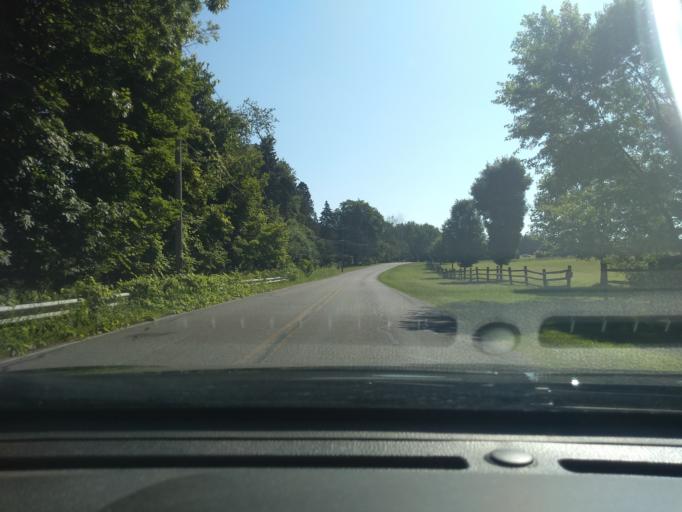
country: US
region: New York
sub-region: Erie County
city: Billington Heights
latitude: 42.7783
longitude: -78.6791
